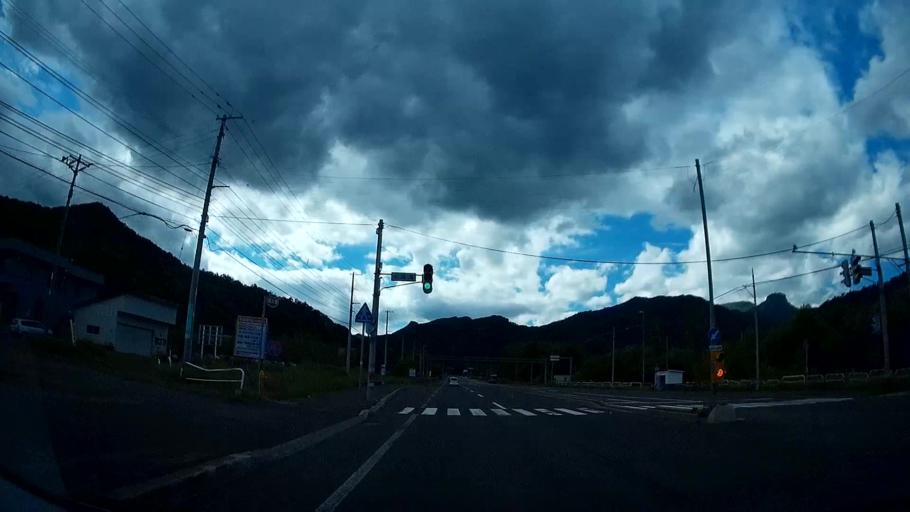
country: JP
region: Hokkaido
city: Sapporo
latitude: 42.9662
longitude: 141.2183
